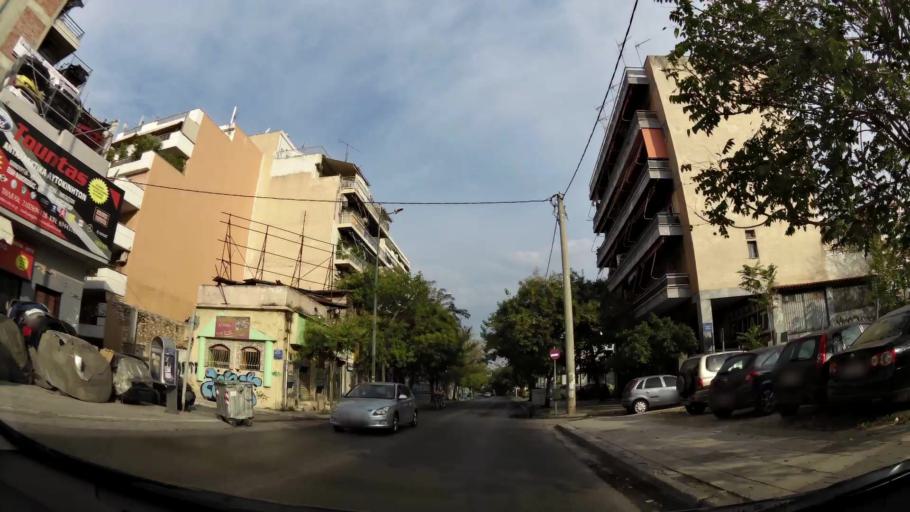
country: GR
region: Attica
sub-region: Nomarchia Athinas
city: Kipseli
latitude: 38.0079
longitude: 23.7221
